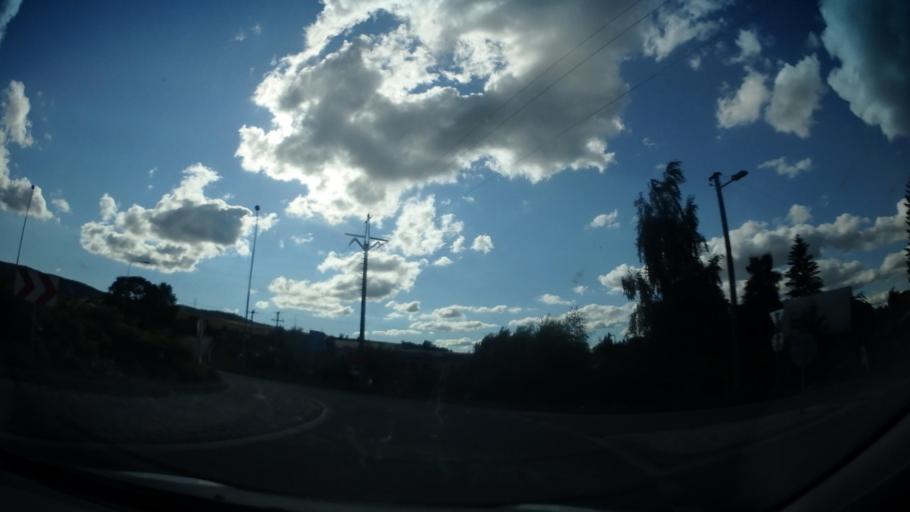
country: CZ
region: South Moravian
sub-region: Okres Blansko
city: Rajec-Jestrebi
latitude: 49.4043
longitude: 16.6332
